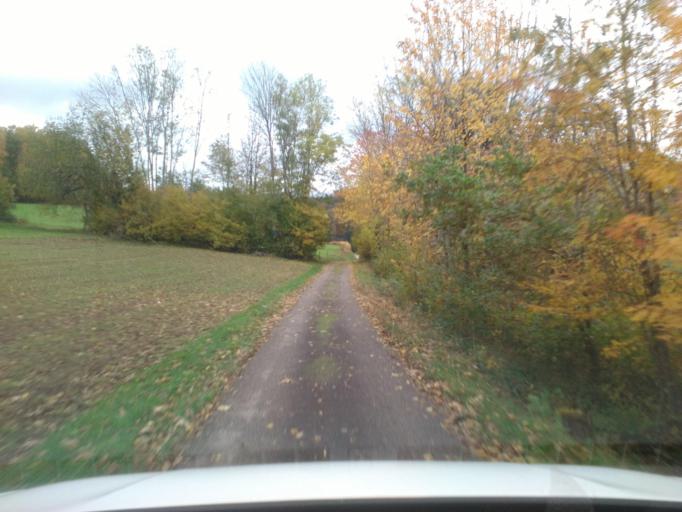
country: FR
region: Lorraine
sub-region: Departement des Vosges
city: Senones
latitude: 48.3386
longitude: 7.0168
